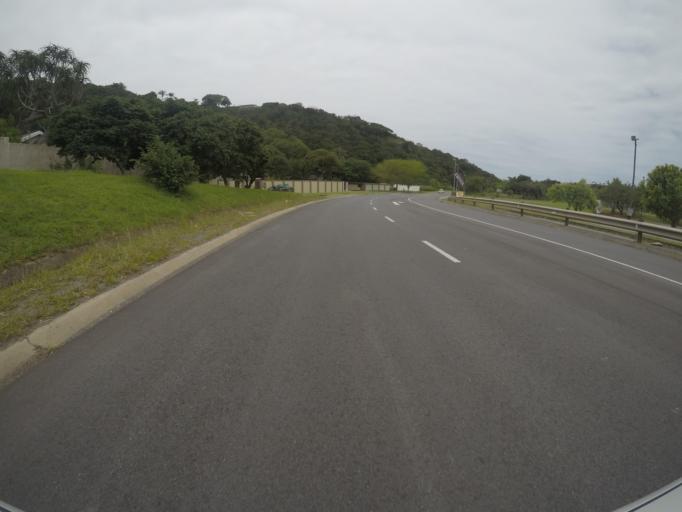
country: ZA
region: Eastern Cape
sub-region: Buffalo City Metropolitan Municipality
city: East London
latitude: -32.9742
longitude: 27.9328
